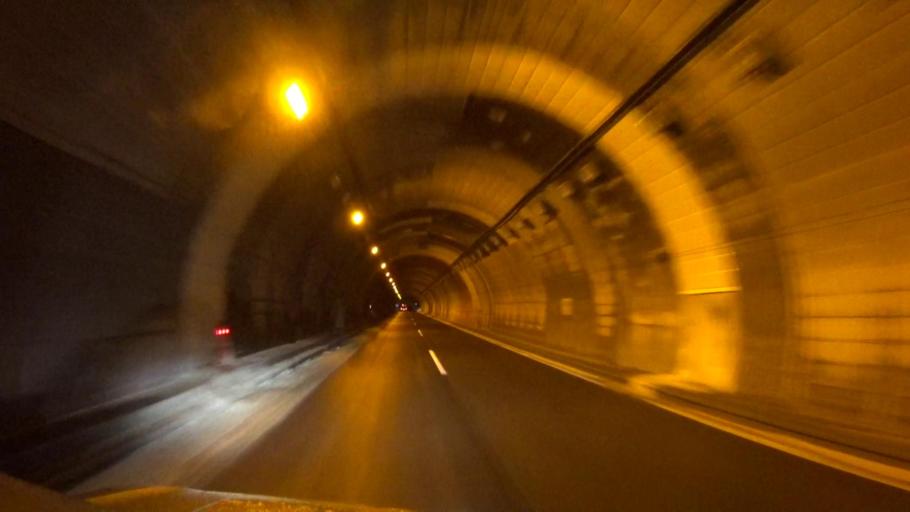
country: JP
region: Hokkaido
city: Otaru
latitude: 43.1751
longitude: 141.0285
